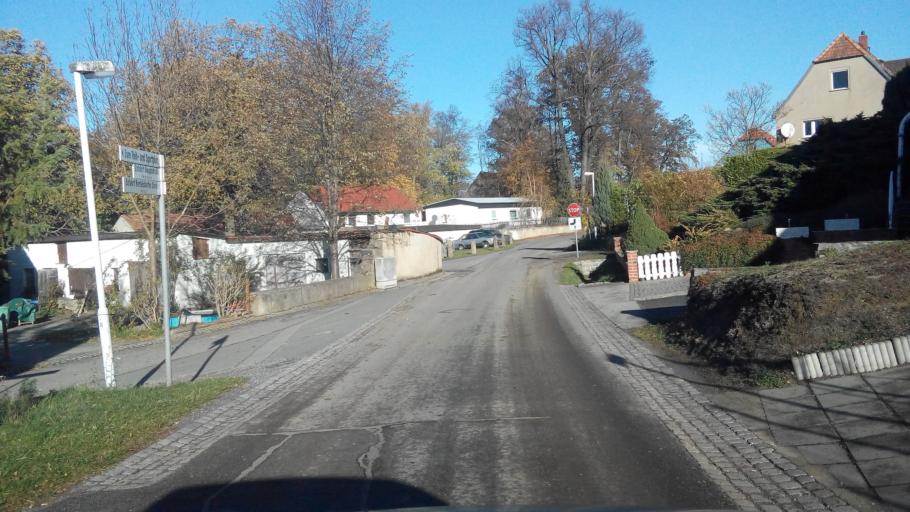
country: DE
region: Saxony
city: Bernstadt
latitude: 51.0655
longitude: 14.7910
